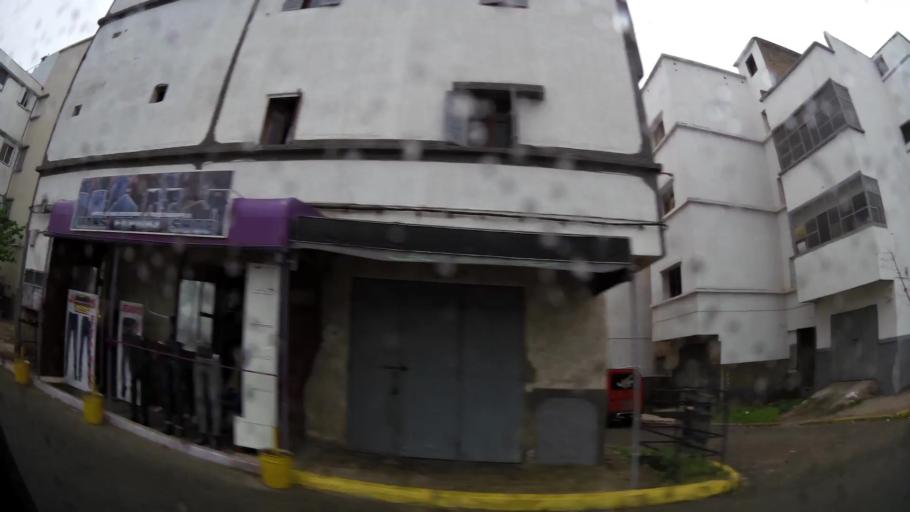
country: MA
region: Grand Casablanca
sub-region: Casablanca
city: Casablanca
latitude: 33.5642
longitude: -7.5593
